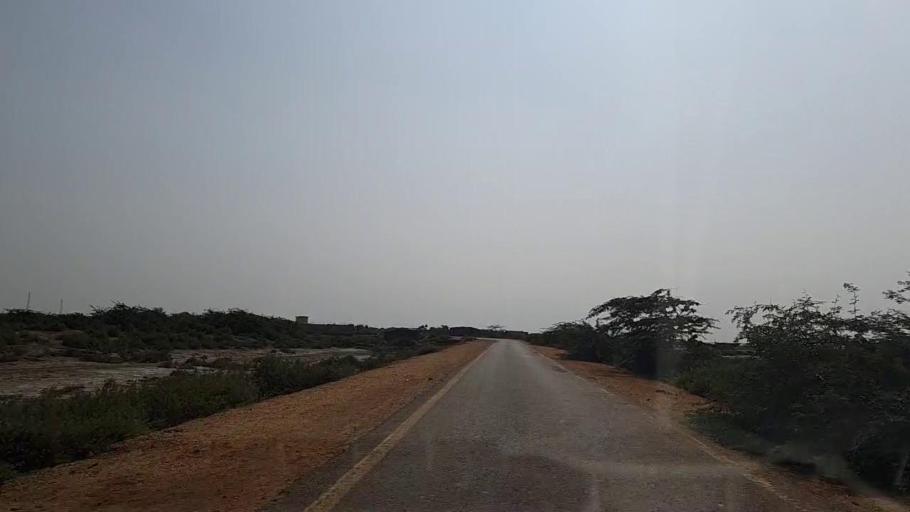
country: PK
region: Sindh
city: Chuhar Jamali
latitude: 24.1777
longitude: 67.8896
